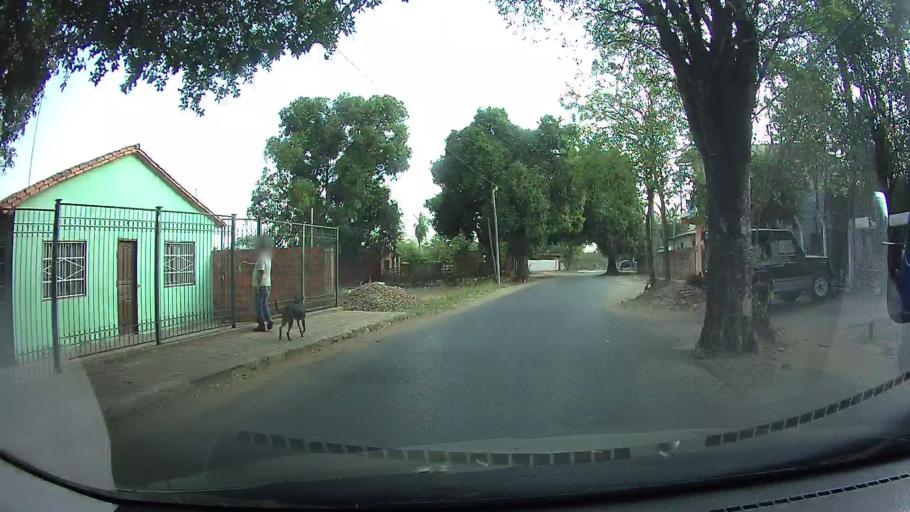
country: PY
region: Central
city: Limpio
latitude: -25.2065
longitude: -57.5076
